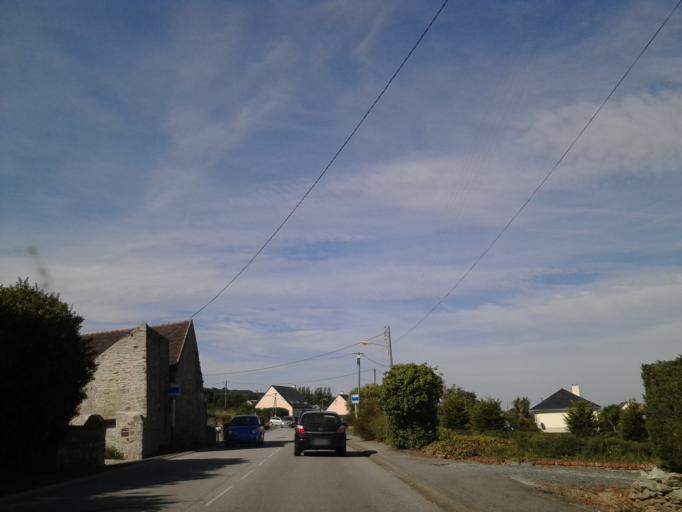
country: FR
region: Lower Normandy
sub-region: Departement de la Manche
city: Tourlaville
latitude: 49.6526
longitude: -1.5540
